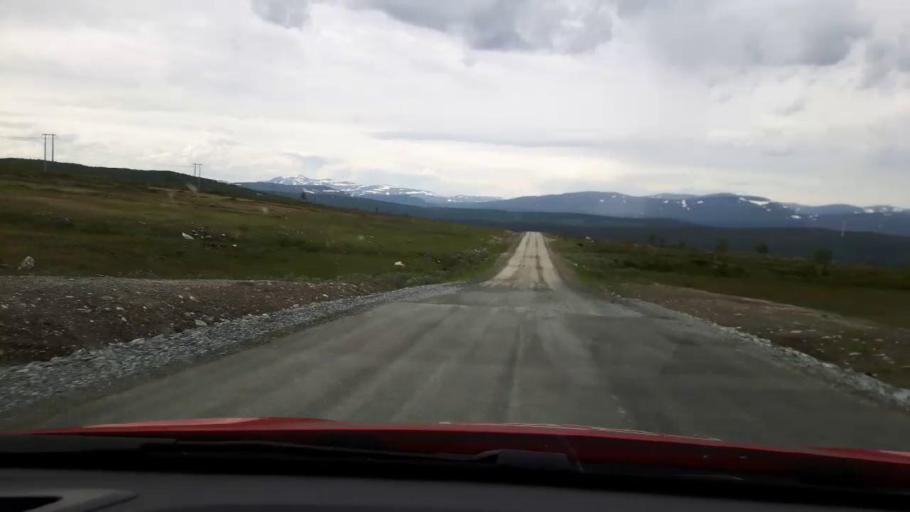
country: SE
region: Jaemtland
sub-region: Are Kommun
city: Are
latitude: 62.7767
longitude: 12.7658
